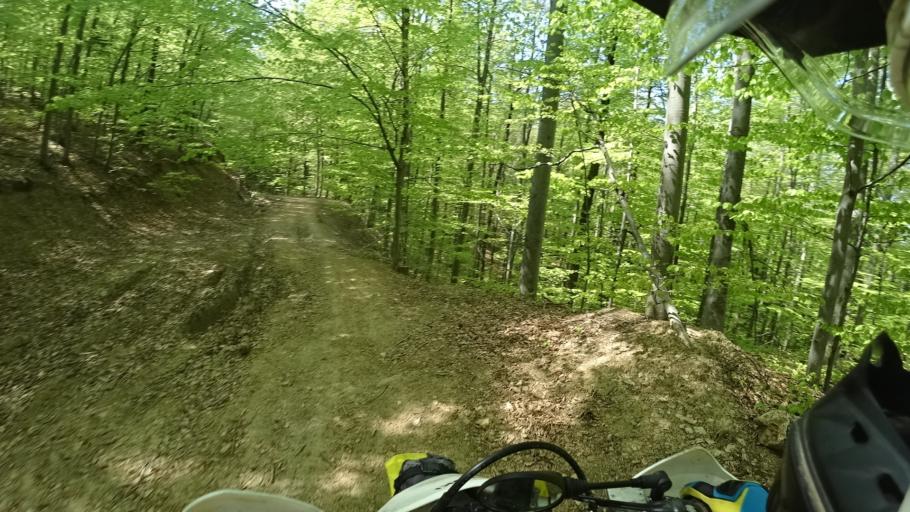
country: HR
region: Zagrebacka
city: Jablanovec
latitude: 45.9052
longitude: 15.9159
